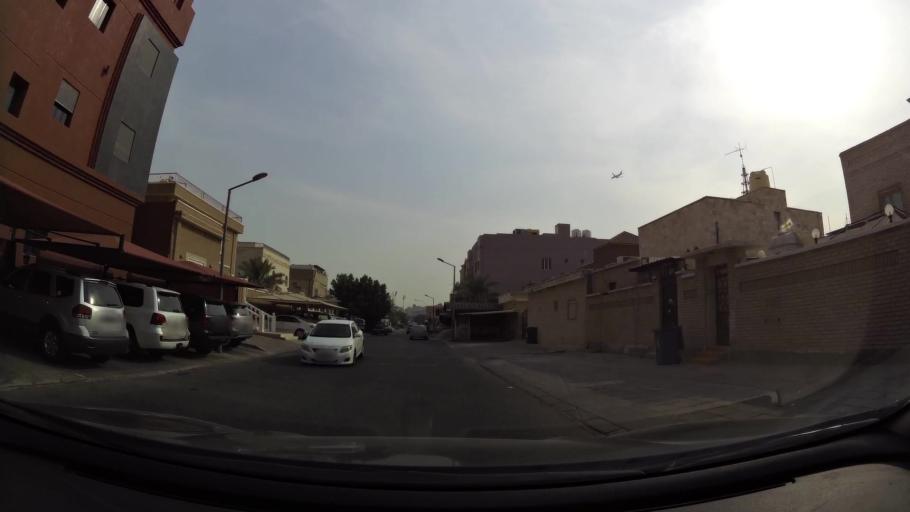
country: KW
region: Al Farwaniyah
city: Al Farwaniyah
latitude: 29.2958
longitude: 47.9622
